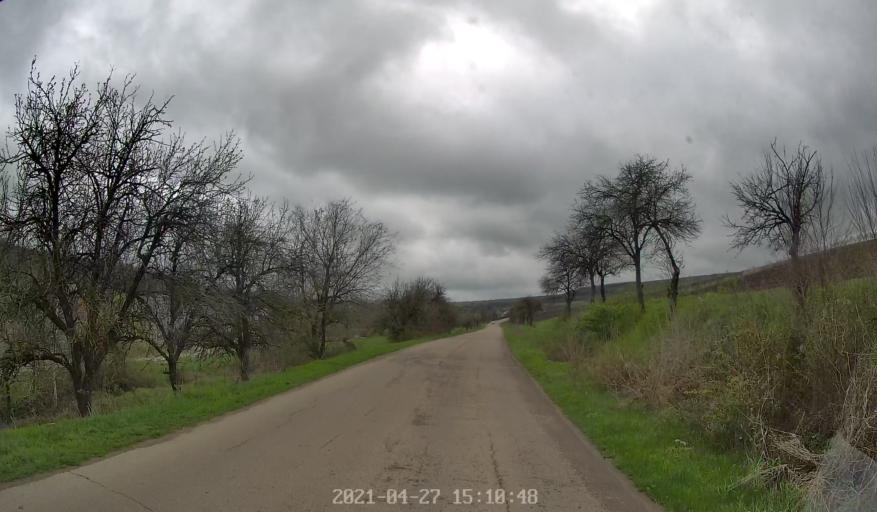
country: MD
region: Chisinau
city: Vadul lui Voda
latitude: 47.0368
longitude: 29.0319
